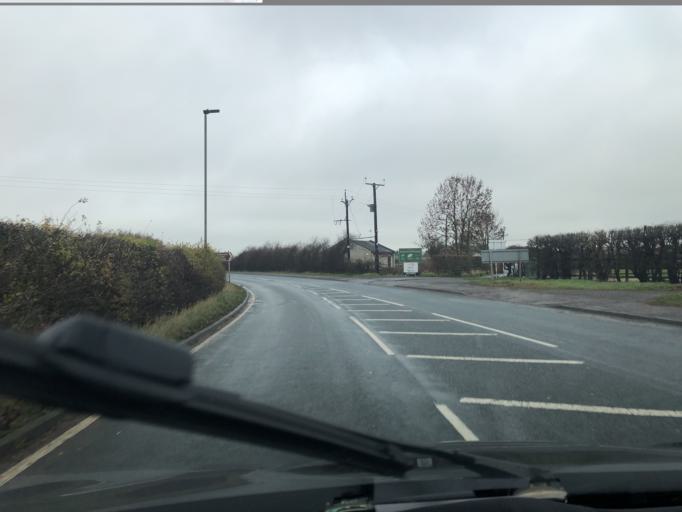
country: GB
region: England
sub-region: North Yorkshire
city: Stokesley
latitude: 54.4654
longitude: -1.1726
